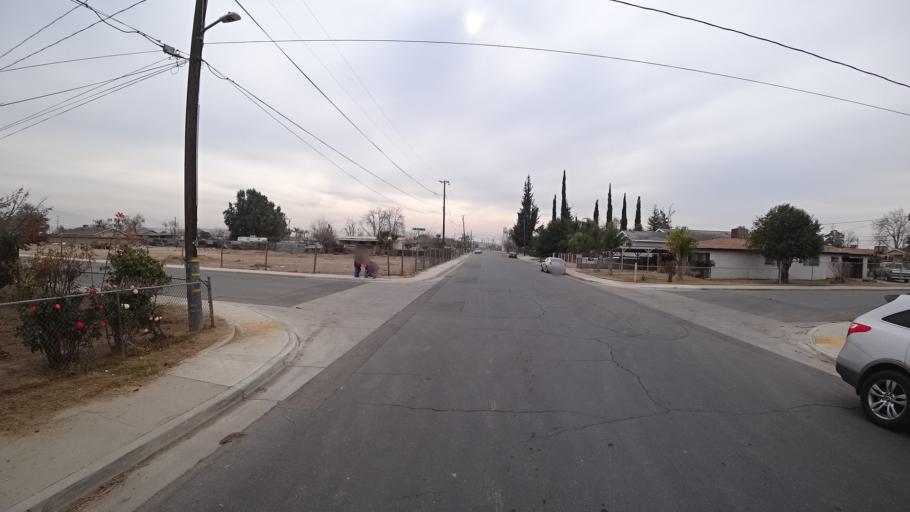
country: US
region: California
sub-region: Kern County
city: Bakersfield
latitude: 35.3638
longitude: -118.9814
